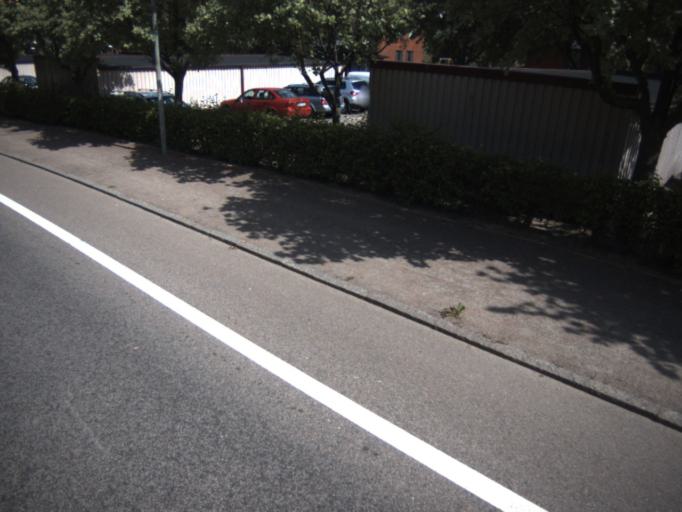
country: SE
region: Skane
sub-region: Helsingborg
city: Helsingborg
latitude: 56.0587
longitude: 12.7172
